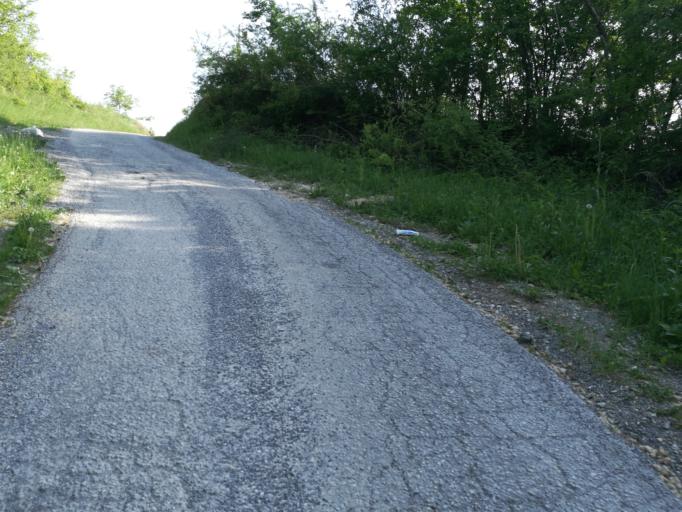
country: HR
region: Krapinsko-Zagorska
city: Radoboj
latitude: 46.2391
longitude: 15.9091
